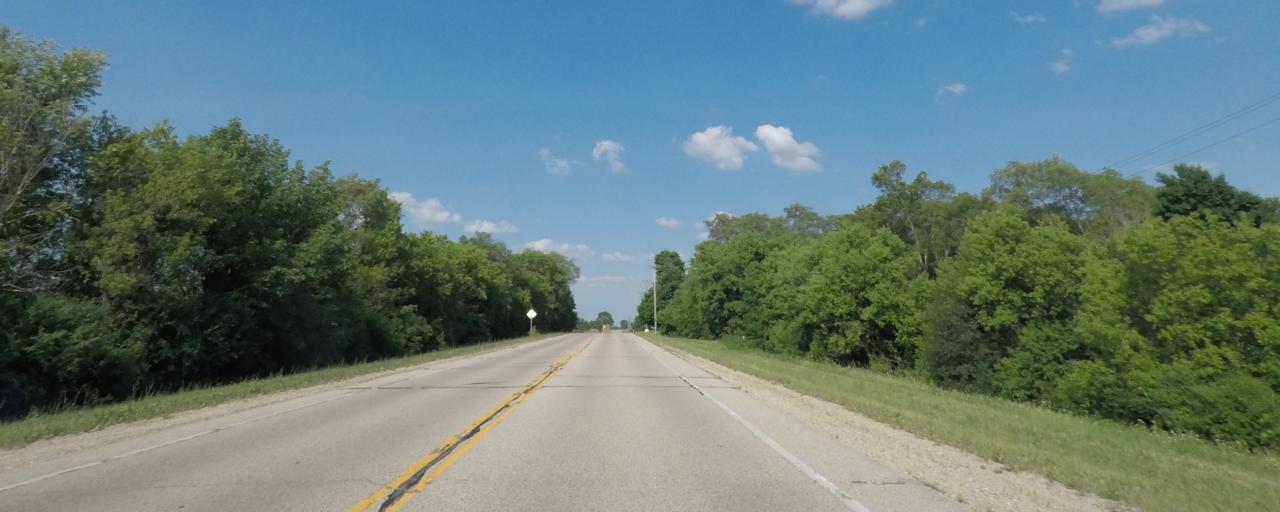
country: US
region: Wisconsin
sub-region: Walworth County
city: East Troy
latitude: 42.8006
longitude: -88.3767
